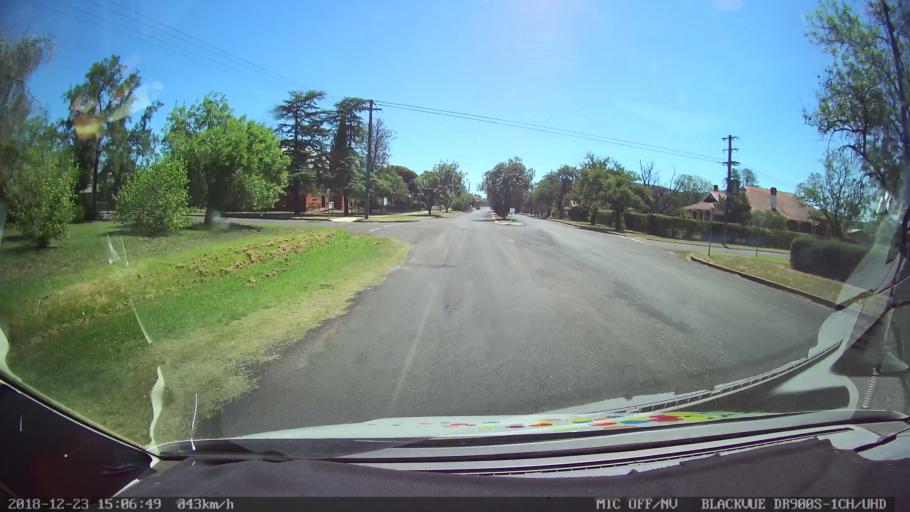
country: AU
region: New South Wales
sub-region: Tamworth Municipality
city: Manilla
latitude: -30.7461
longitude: 150.7257
